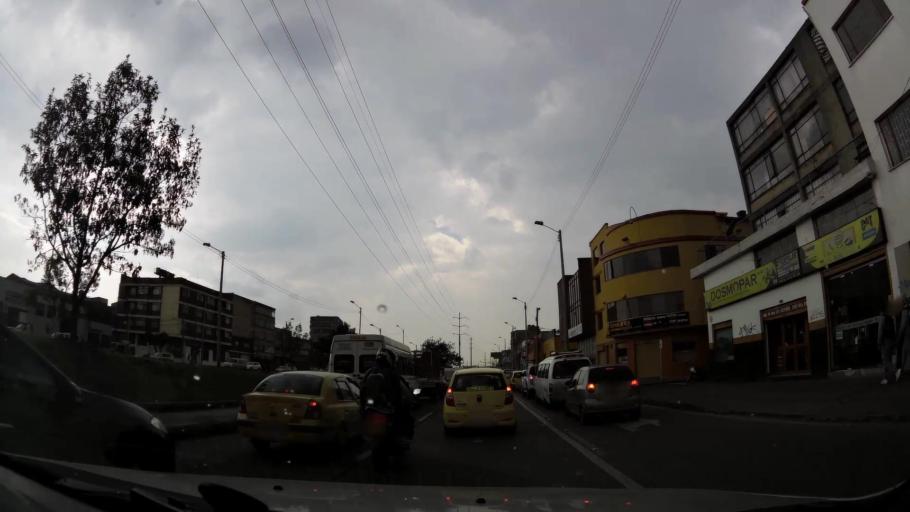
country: CO
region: Bogota D.C.
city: Bogota
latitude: 4.6019
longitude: -74.0915
